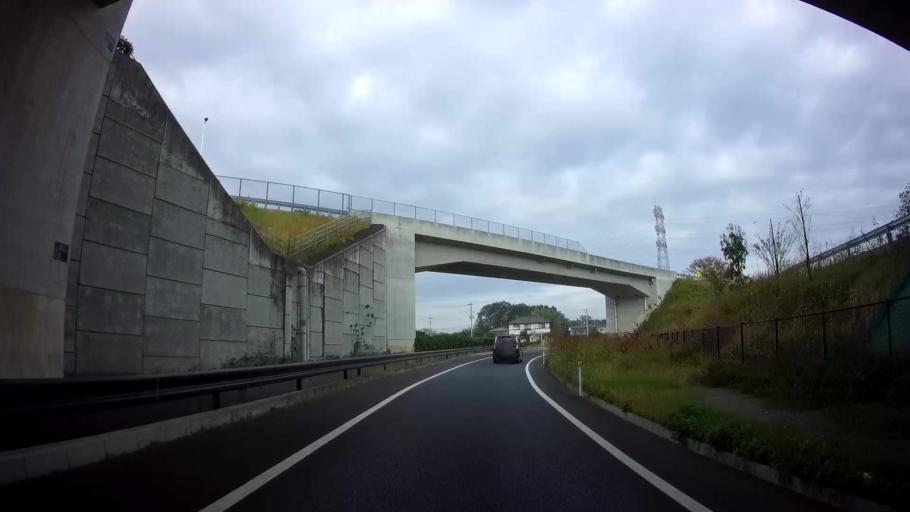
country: JP
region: Saitama
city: Okegawa
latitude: 36.0011
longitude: 139.5186
